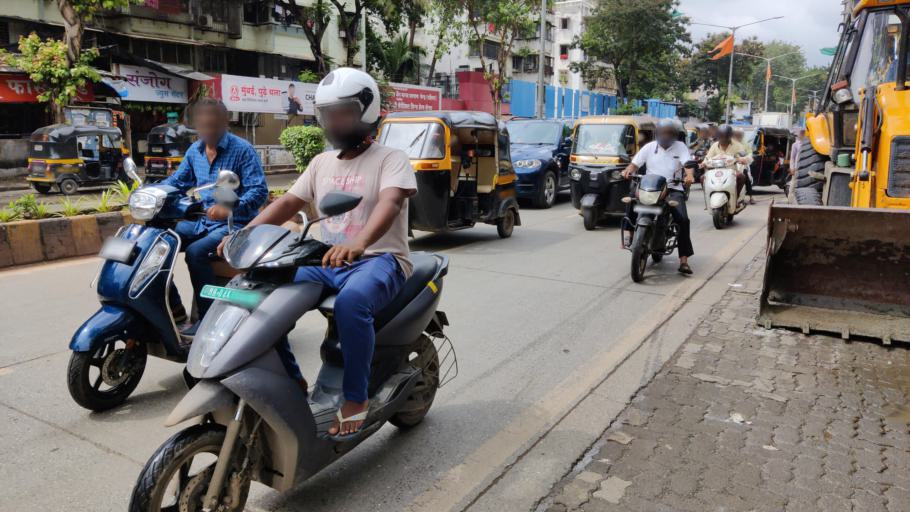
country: IN
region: Maharashtra
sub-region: Mumbai Suburban
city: Borivli
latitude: 19.2460
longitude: 72.8610
